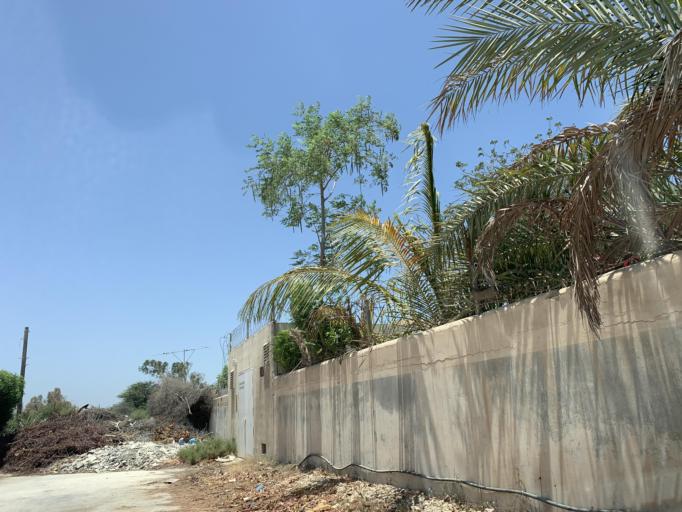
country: BH
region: Manama
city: Jidd Hafs
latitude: 26.2196
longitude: 50.4775
